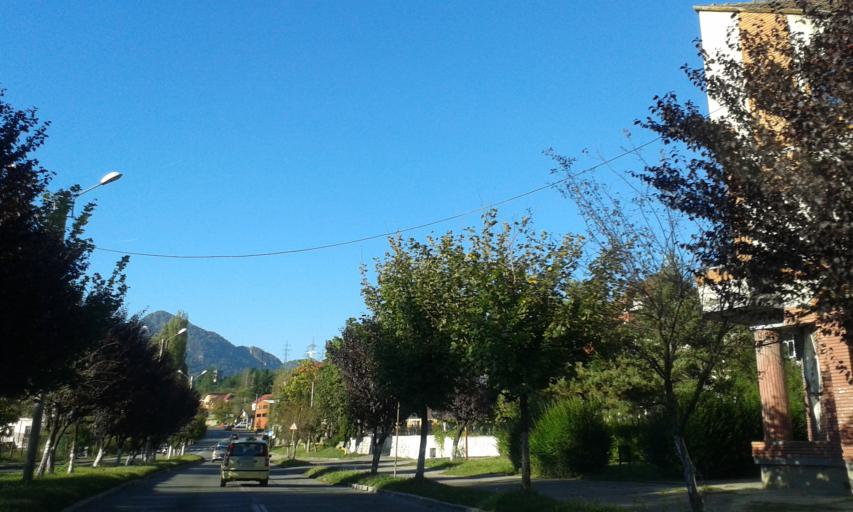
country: RO
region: Hunedoara
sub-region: Municipiul Petrosani
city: Petrosani
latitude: 45.4244
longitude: 23.3678
